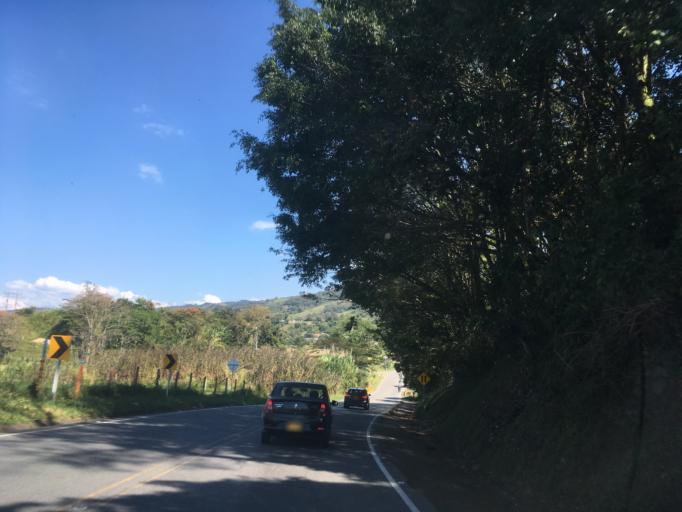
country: CO
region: Santander
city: Suaita
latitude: 6.0669
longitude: -73.4233
